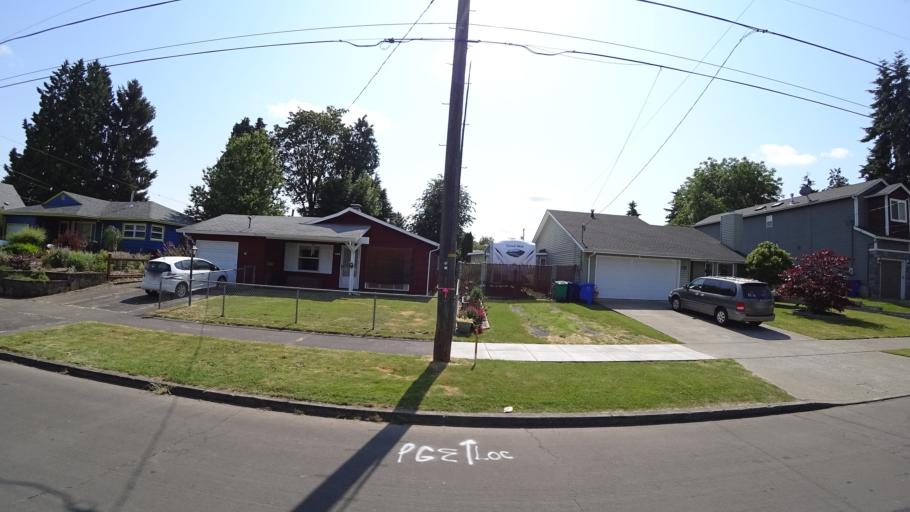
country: US
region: Oregon
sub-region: Washington County
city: West Haven
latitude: 45.5983
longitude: -122.7450
